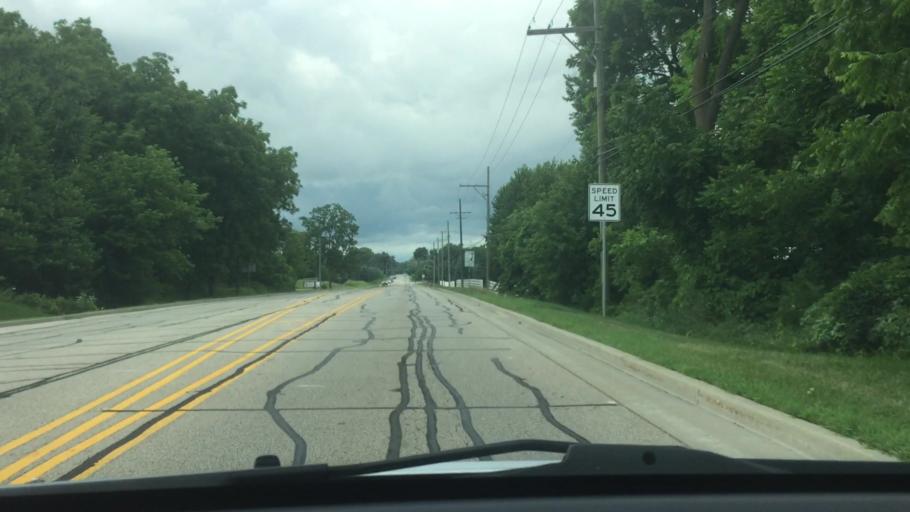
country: US
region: Illinois
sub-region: McHenry County
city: Crystal Lake
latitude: 42.2769
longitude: -88.3208
